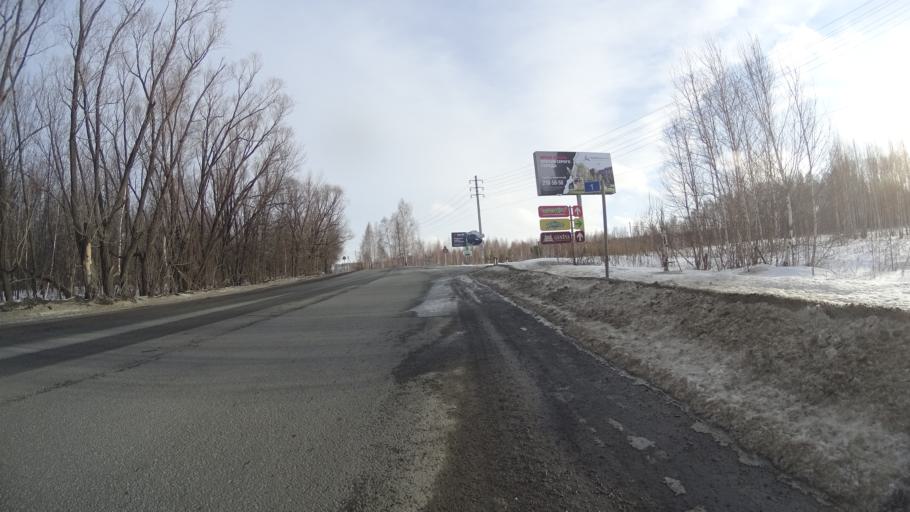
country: RU
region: Chelyabinsk
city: Sargazy
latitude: 55.1367
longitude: 61.2830
